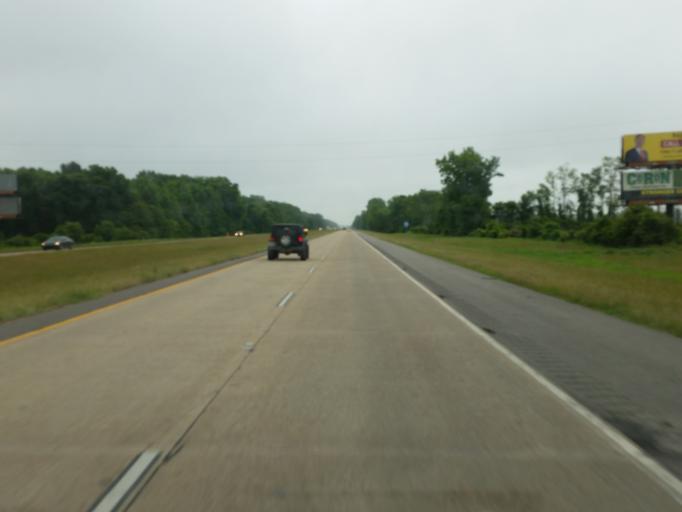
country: US
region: Louisiana
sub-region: Madison Parish
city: Tallulah
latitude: 32.3779
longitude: -91.1642
